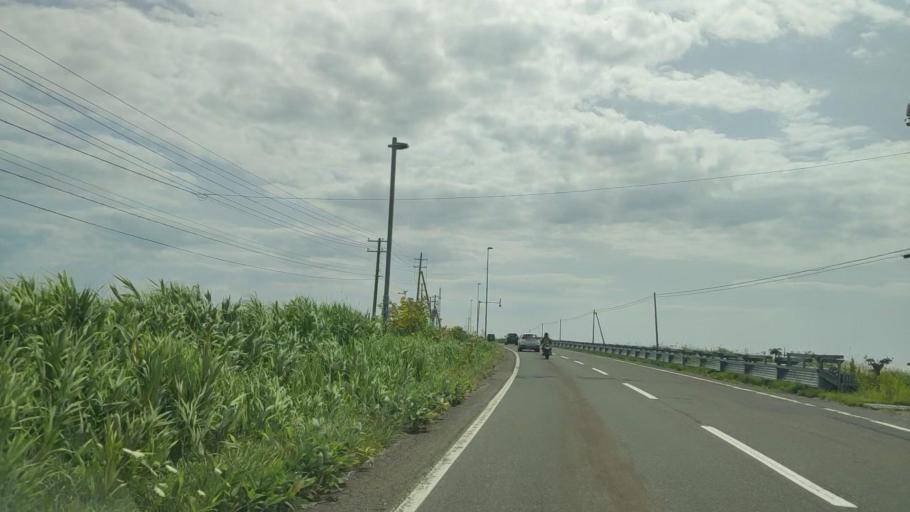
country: JP
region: Hokkaido
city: Rumoi
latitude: 44.4429
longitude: 141.7537
